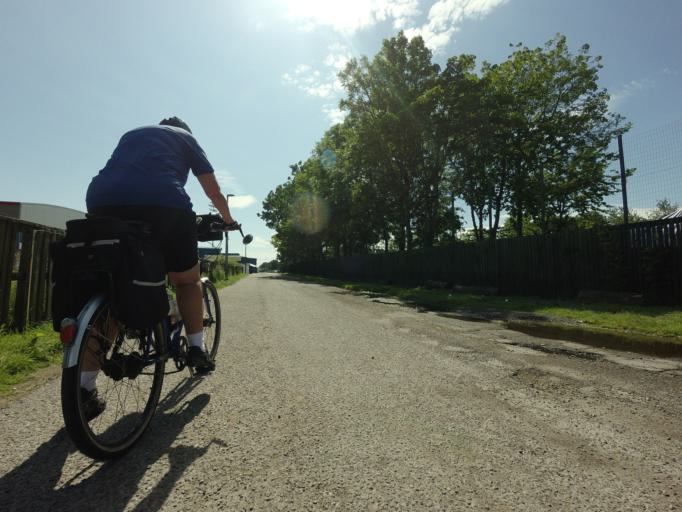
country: GB
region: Scotland
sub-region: Highland
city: Dingwall
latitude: 57.5969
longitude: -4.4193
